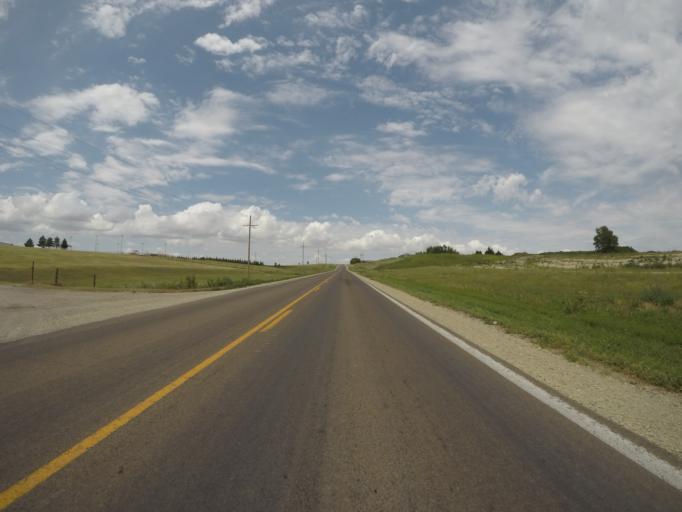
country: US
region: Kansas
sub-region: Rawlins County
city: Atwood
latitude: 39.8256
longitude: -101.0468
